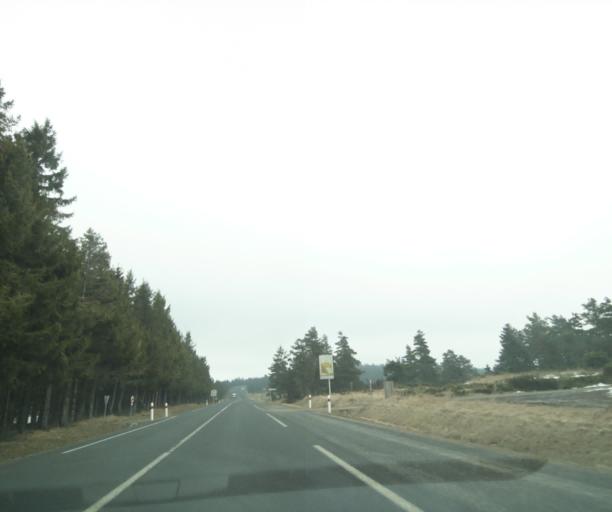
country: FR
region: Languedoc-Roussillon
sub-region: Departement de la Lozere
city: Langogne
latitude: 44.7531
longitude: 3.9573
